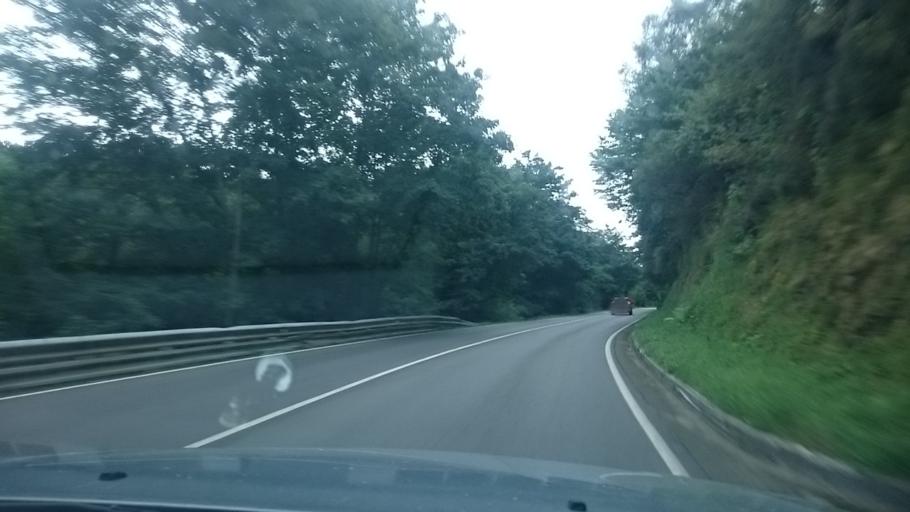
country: ES
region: Asturias
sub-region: Province of Asturias
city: Carrena
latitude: 43.4131
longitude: -4.8856
